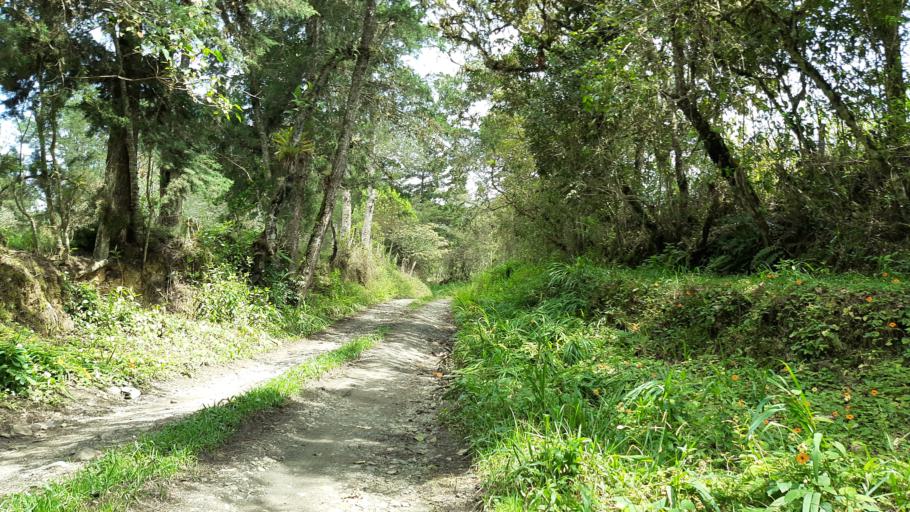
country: CO
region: Boyaca
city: Garagoa
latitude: 5.0527
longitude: -73.3541
